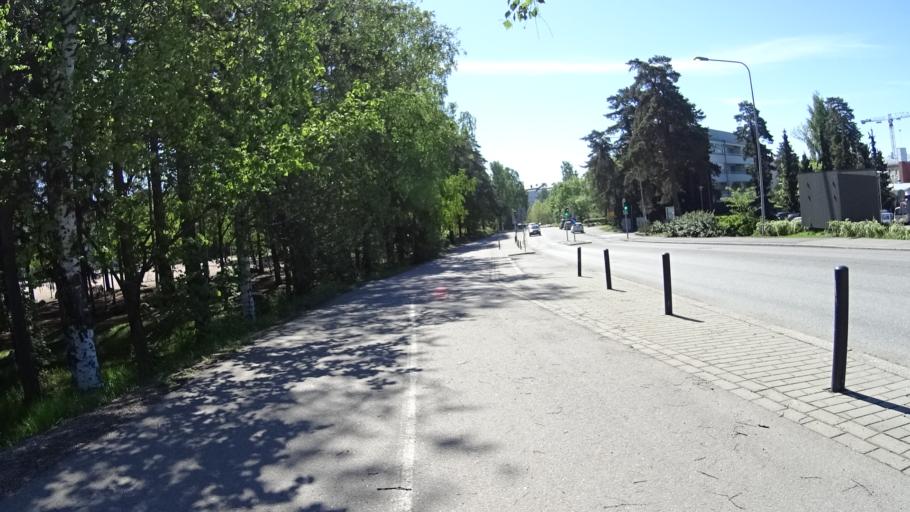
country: FI
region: Uusimaa
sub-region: Helsinki
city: Teekkarikylae
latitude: 60.2024
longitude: 24.8733
